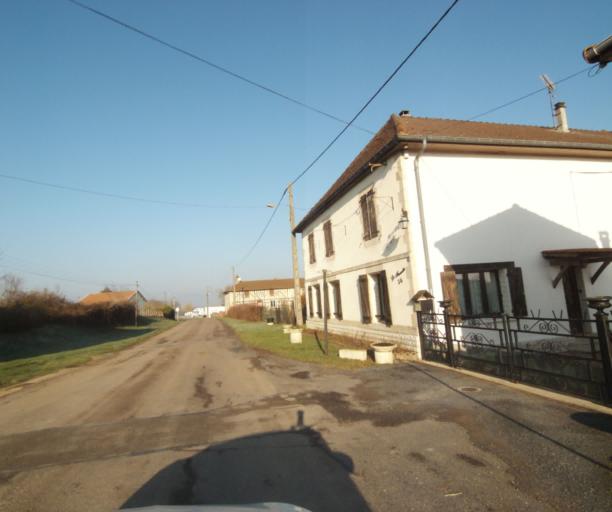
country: FR
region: Champagne-Ardenne
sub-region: Departement de la Haute-Marne
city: Montier-en-Der
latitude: 48.4814
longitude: 4.7503
